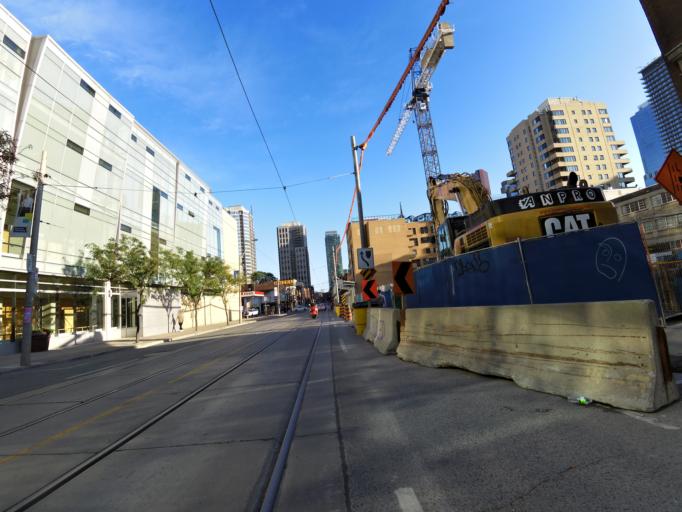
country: CA
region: Ontario
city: Toronto
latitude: 43.6574
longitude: -79.3776
